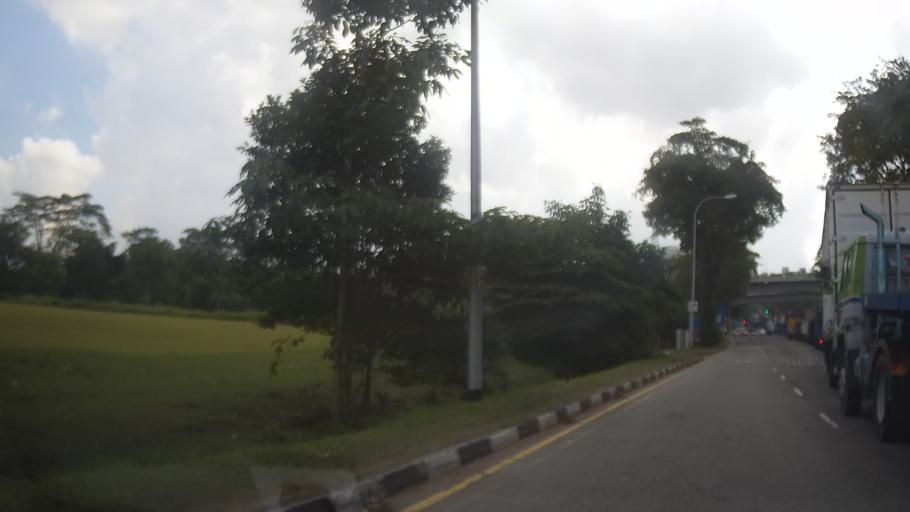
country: MY
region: Johor
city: Johor Bahru
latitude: 1.4393
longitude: 103.7668
